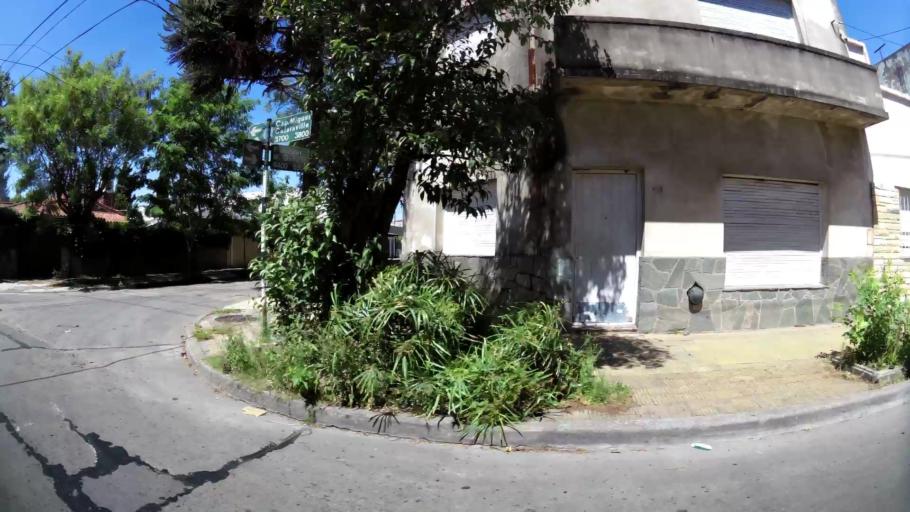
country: AR
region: Buenos Aires
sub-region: Partido de General San Martin
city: General San Martin
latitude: -34.5288
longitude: -58.5443
